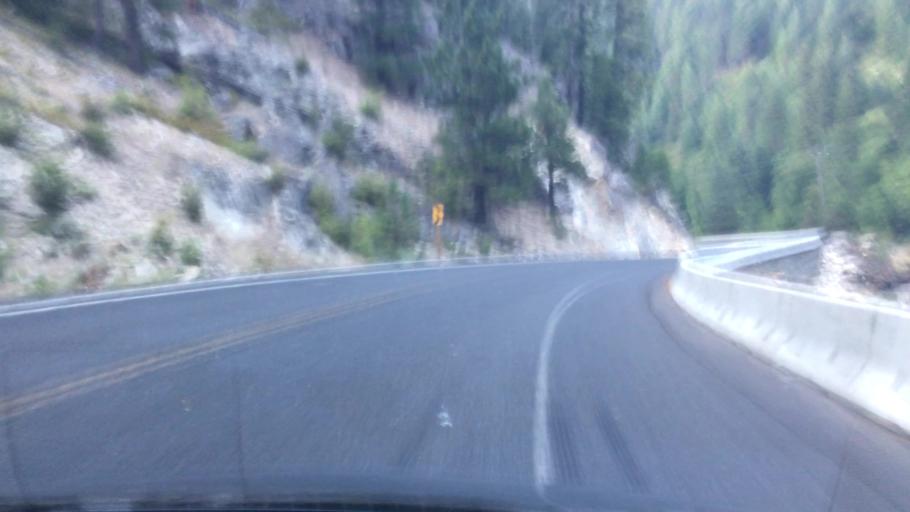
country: US
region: Idaho
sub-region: Valley County
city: McCall
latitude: 45.1340
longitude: -116.2845
